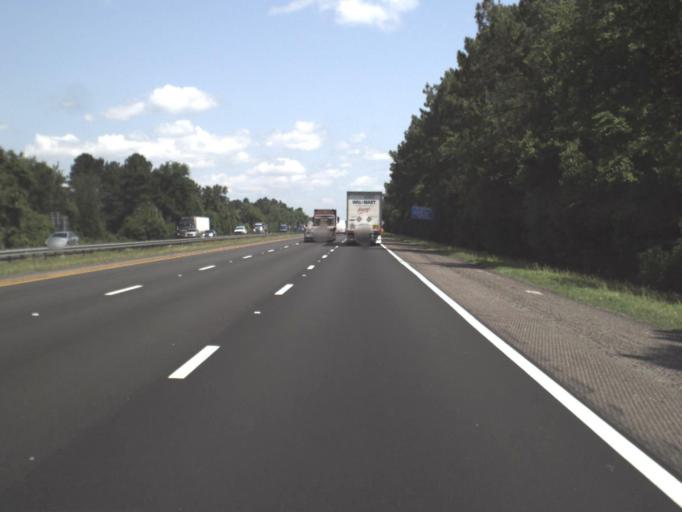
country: US
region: Florida
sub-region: Nassau County
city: Yulee
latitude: 30.5578
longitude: -81.6413
